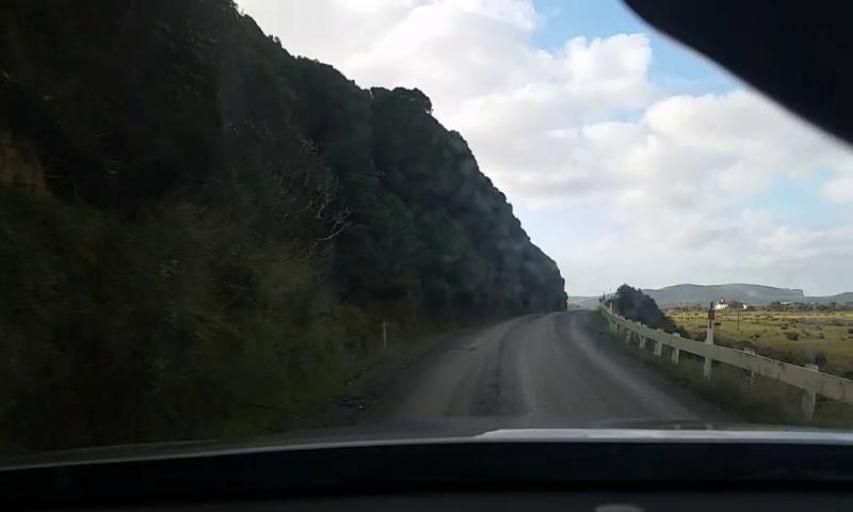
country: NZ
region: Otago
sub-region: Clutha District
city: Papatowai
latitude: -46.6521
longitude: 169.0949
